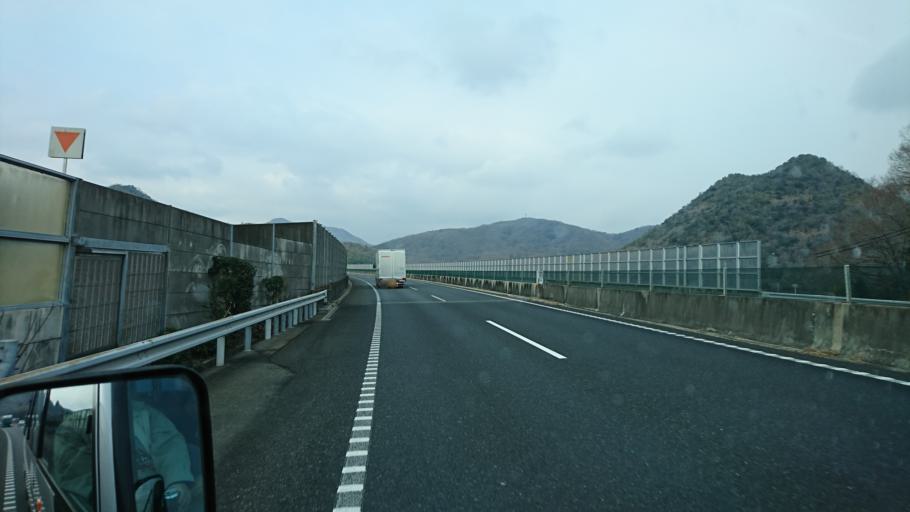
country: JP
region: Hyogo
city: Himeji
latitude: 34.8543
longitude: 134.7845
